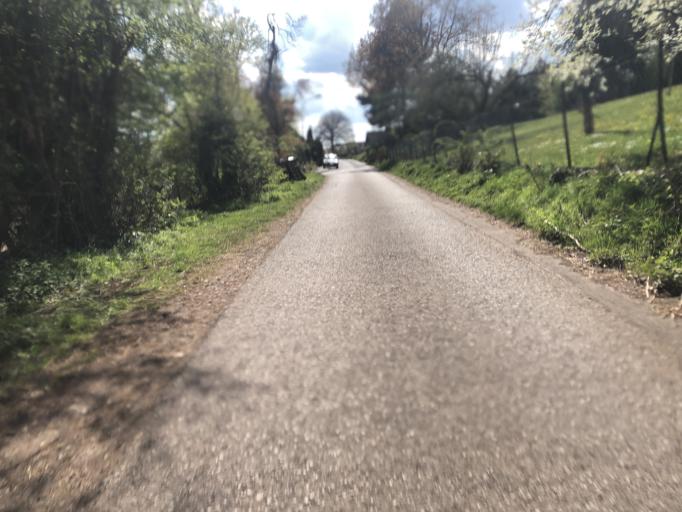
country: DE
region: North Rhine-Westphalia
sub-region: Regierungsbezirk Koln
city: Mechernich
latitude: 50.6272
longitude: 6.6205
